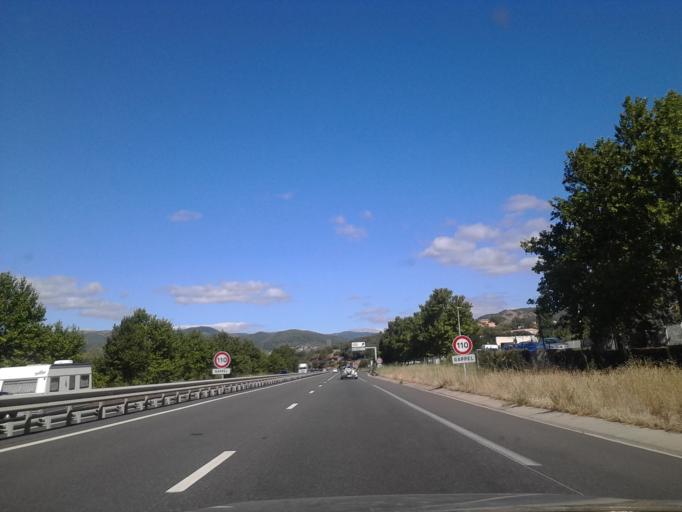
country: FR
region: Languedoc-Roussillon
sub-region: Departement de l'Herault
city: Lodeve
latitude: 43.6889
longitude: 3.3532
